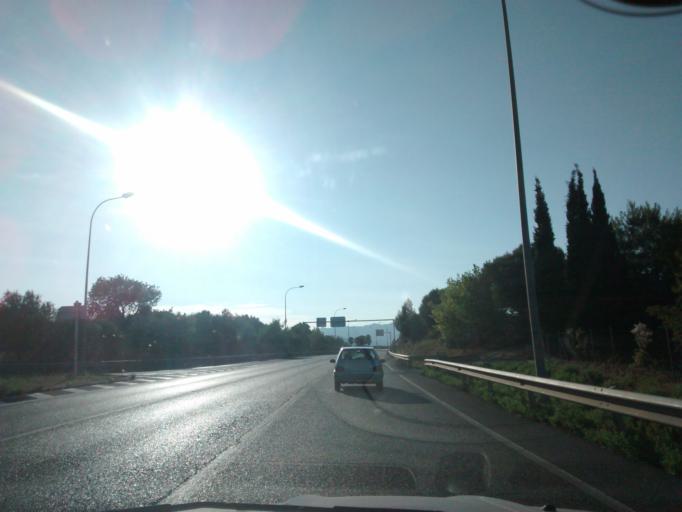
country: ES
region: Balearic Islands
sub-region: Illes Balears
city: Alcudia
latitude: 39.8428
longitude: 3.0979
